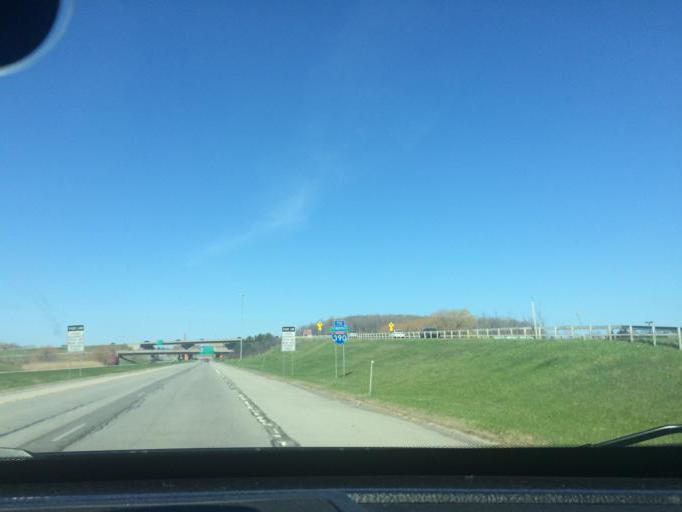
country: US
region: New York
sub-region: Monroe County
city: Rochester
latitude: 43.1096
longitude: -77.5934
